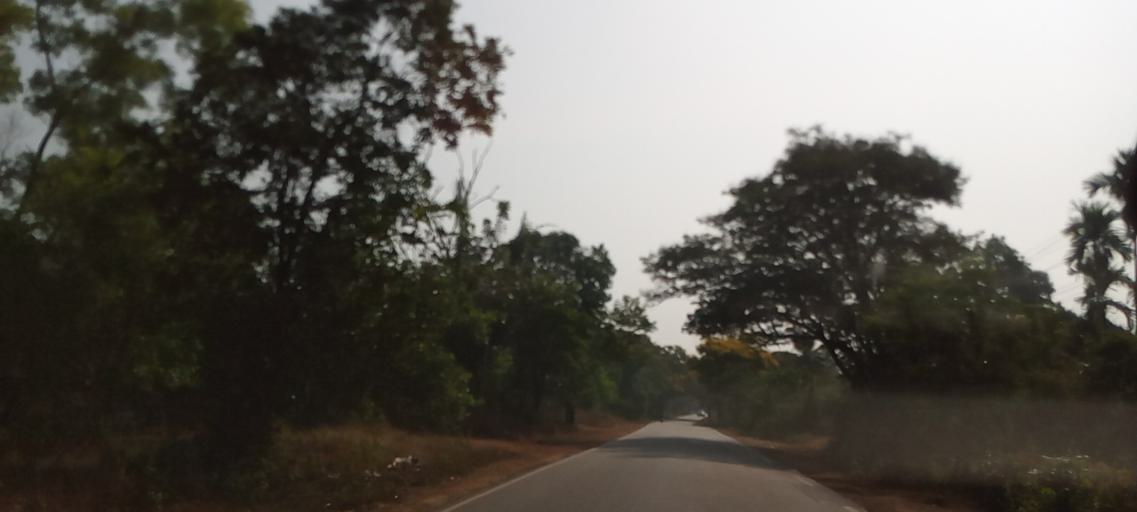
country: IN
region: Karnataka
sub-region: Udupi
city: Coondapoor
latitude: 13.5117
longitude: 74.7787
